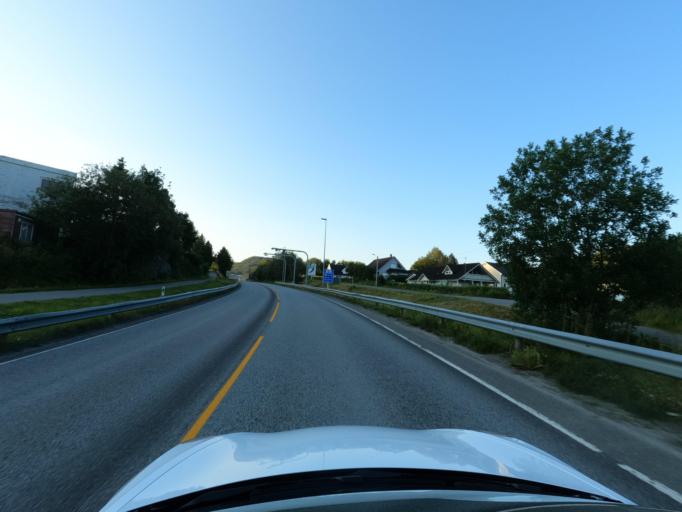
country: NO
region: Troms
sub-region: Harstad
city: Harstad
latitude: 68.7758
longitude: 16.5633
